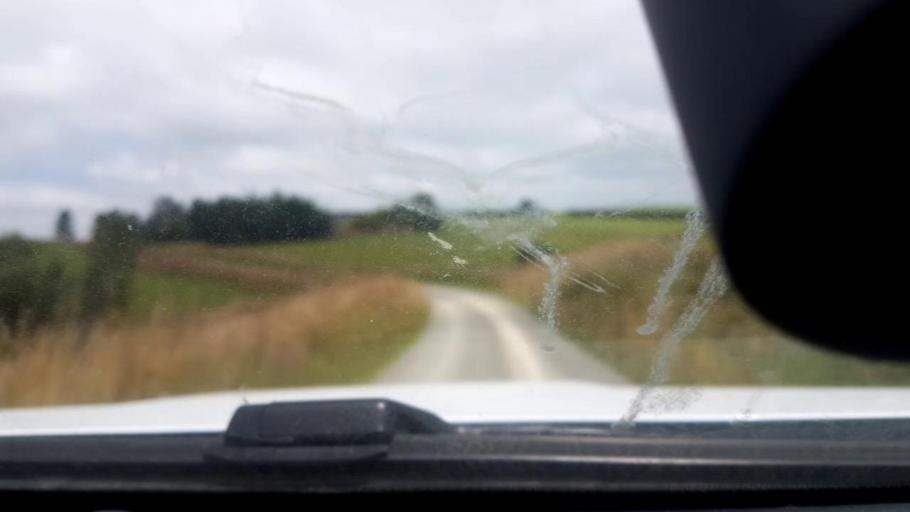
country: NZ
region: Canterbury
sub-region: Timaru District
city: Pleasant Point
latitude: -44.1595
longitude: 171.1464
